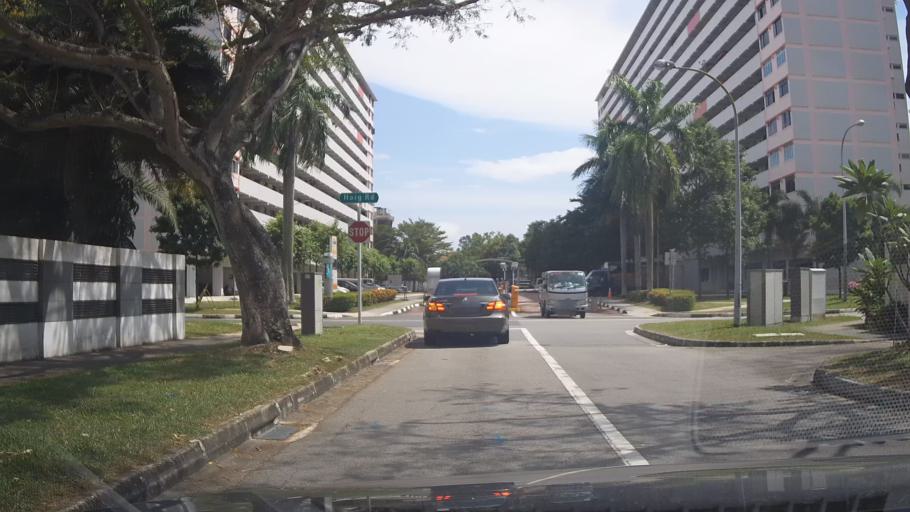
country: SG
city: Singapore
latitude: 1.3110
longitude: 103.8966
